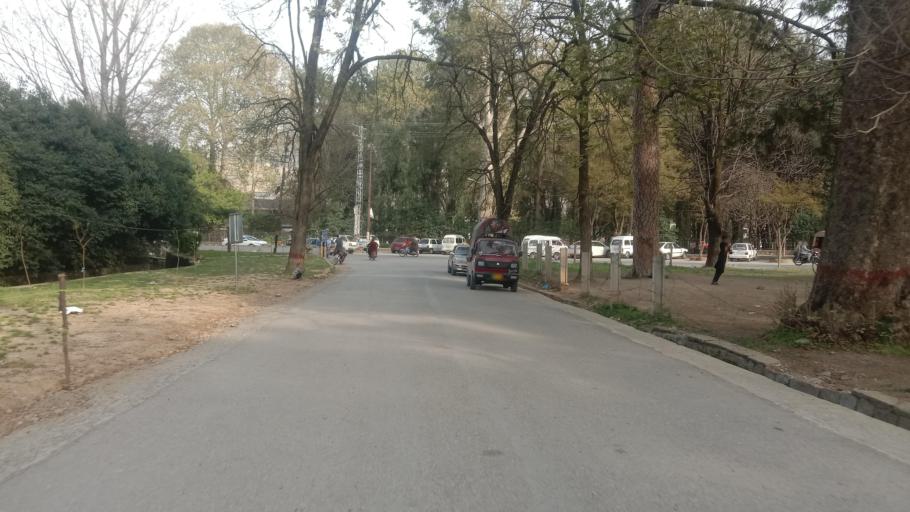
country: PK
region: Khyber Pakhtunkhwa
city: Abbottabad
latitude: 34.1513
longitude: 73.2151
